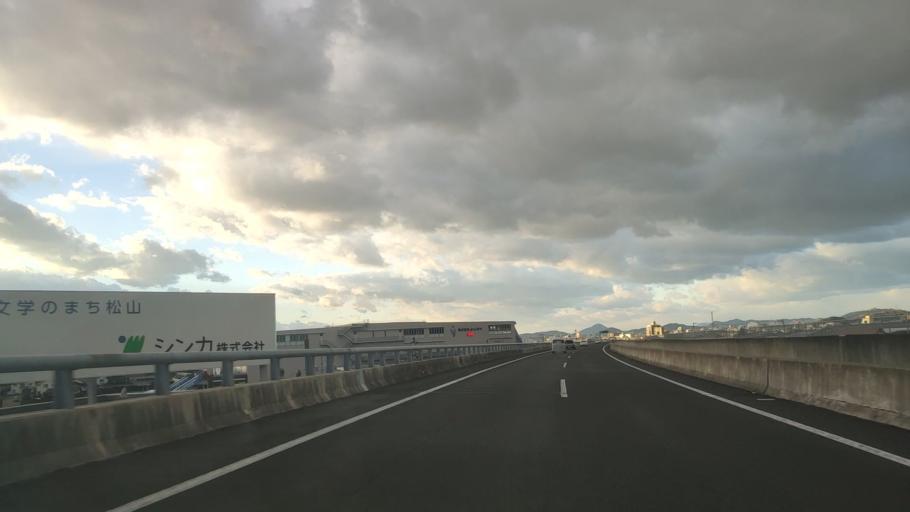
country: JP
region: Ehime
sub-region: Shikoku-chuo Shi
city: Matsuyama
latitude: 33.7893
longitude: 132.8062
